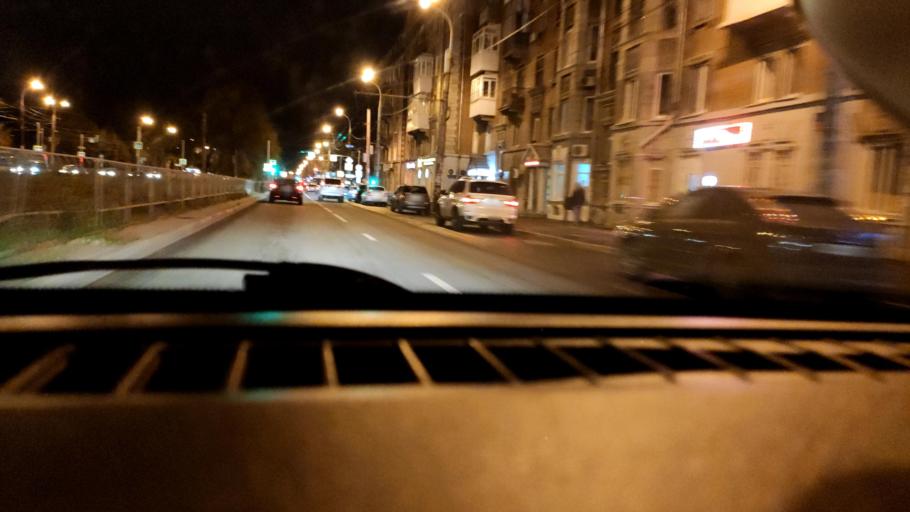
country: RU
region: Samara
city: Samara
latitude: 53.2145
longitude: 50.2525
